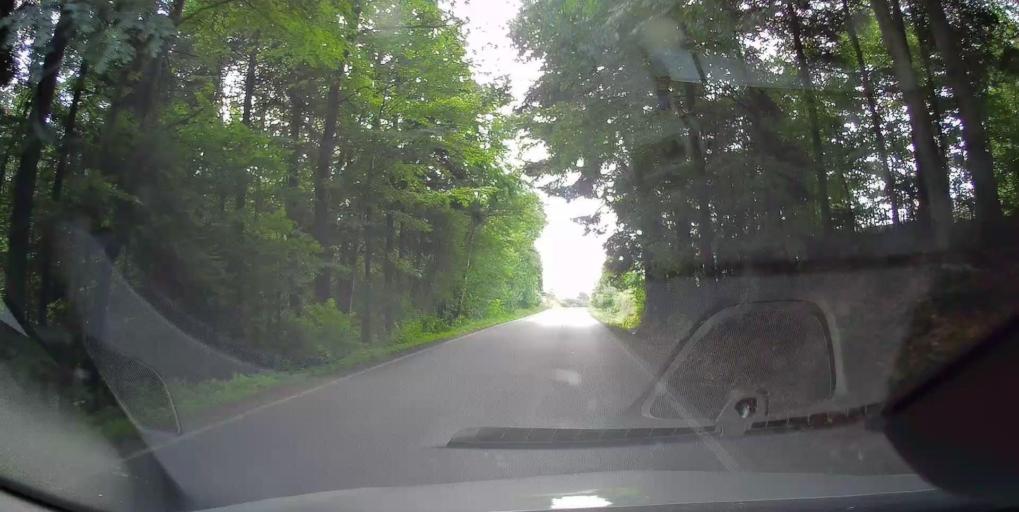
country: PL
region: Lesser Poland Voivodeship
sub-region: Powiat nowosadecki
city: Korzenna
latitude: 49.6958
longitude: 20.7663
